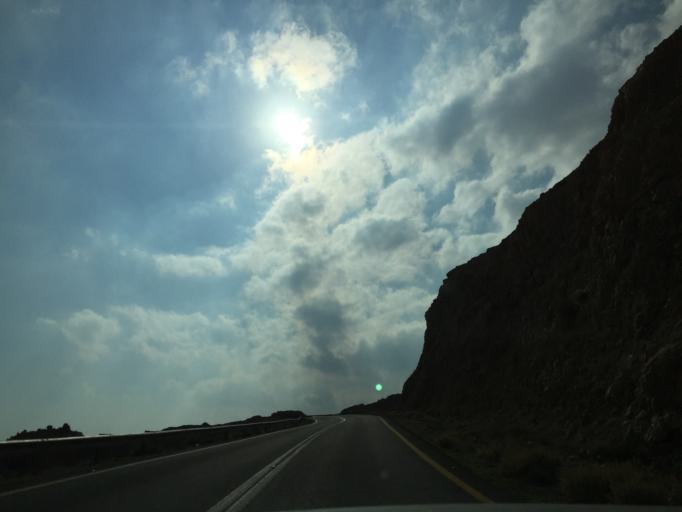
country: IL
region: Southern District
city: `En Boqeq
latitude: 31.3197
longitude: 35.3324
